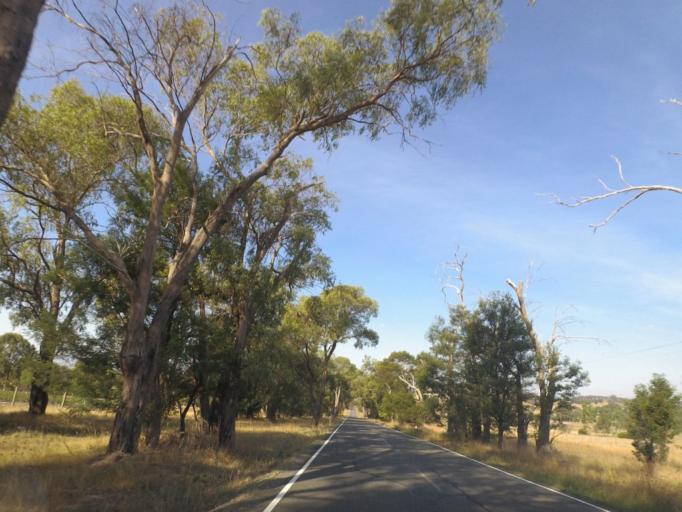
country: AU
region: Victoria
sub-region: Yarra Ranges
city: Lilydale
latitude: -37.7233
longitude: 145.4038
